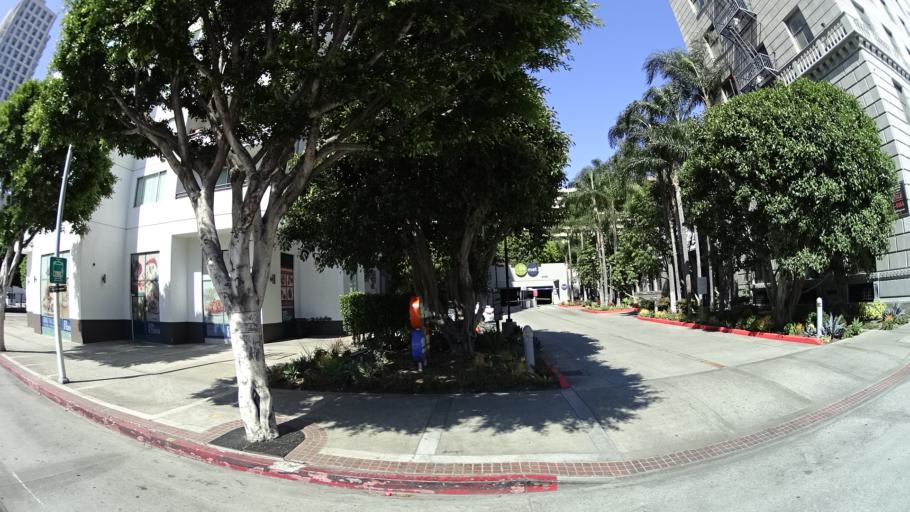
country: US
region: California
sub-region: Los Angeles County
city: Los Angeles
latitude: 34.0441
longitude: -118.2623
